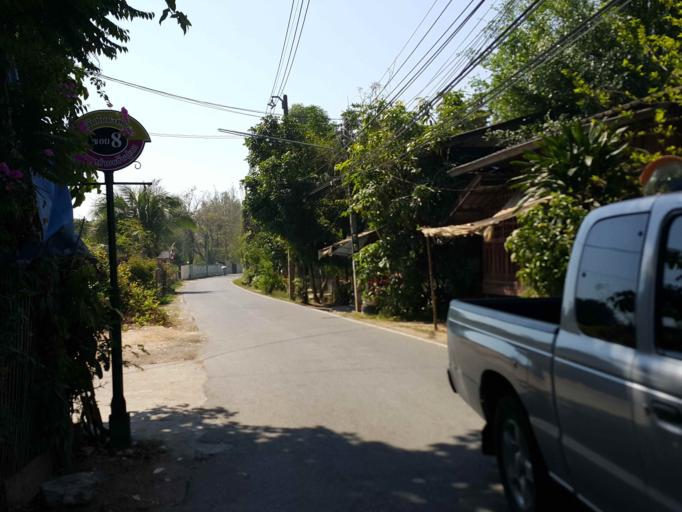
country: TH
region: Chiang Mai
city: San Kamphaeng
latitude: 18.7847
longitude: 99.0817
